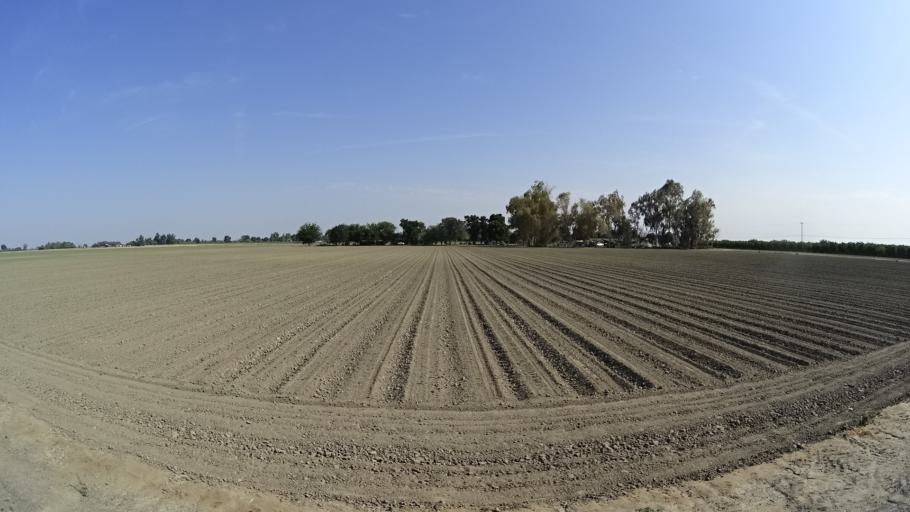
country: US
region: California
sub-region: Kings County
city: Lemoore
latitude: 36.3375
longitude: -119.8528
